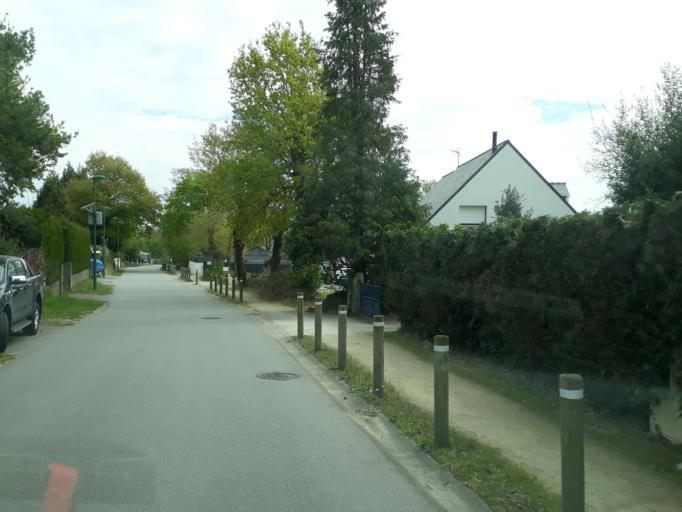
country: FR
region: Brittany
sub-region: Departement du Morbihan
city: Surzur
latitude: 47.5816
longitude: -2.6392
